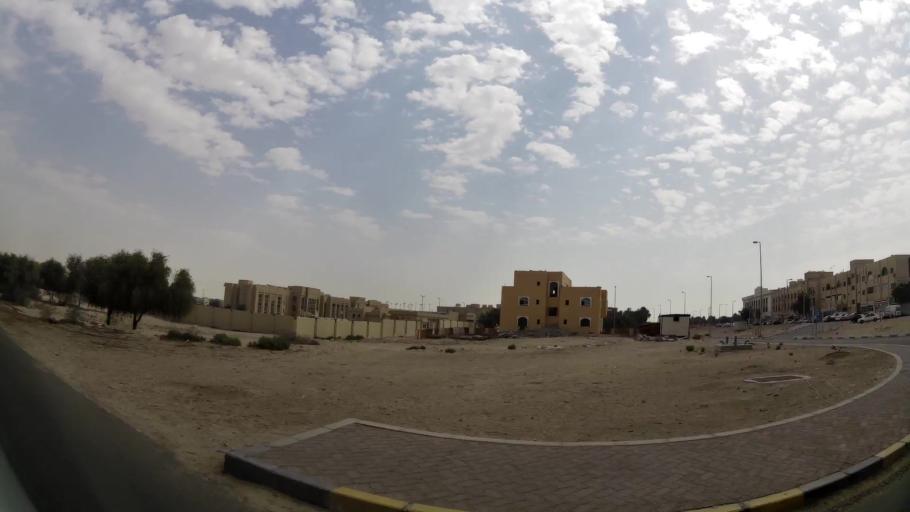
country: AE
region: Abu Dhabi
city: Abu Dhabi
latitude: 24.3056
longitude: 54.6169
